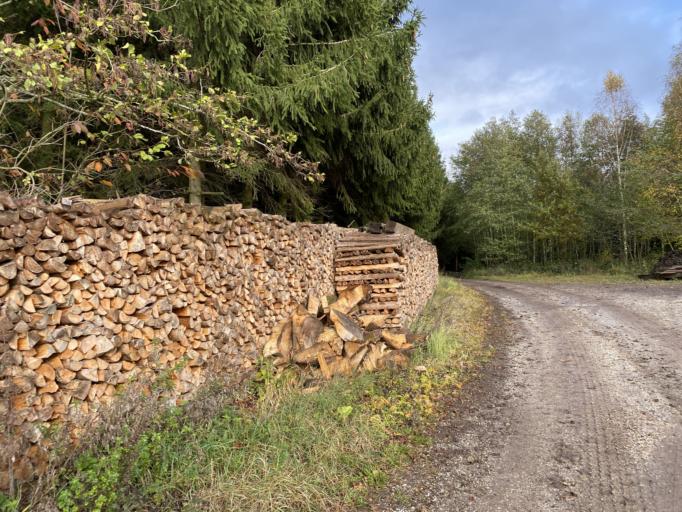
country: DE
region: Bavaria
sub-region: Upper Bavaria
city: Wolfersdorf
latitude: 48.4994
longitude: 11.7085
